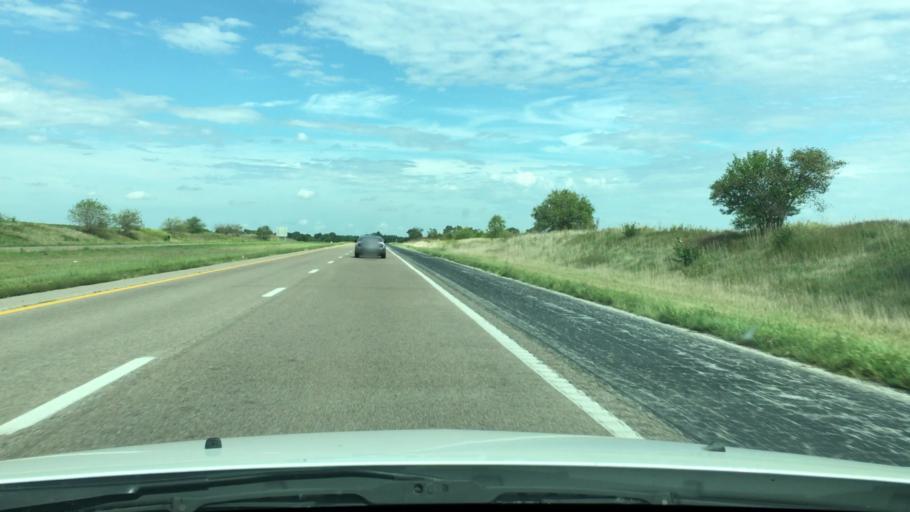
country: US
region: Missouri
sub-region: Audrain County
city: Mexico
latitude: 39.0319
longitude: -91.8871
